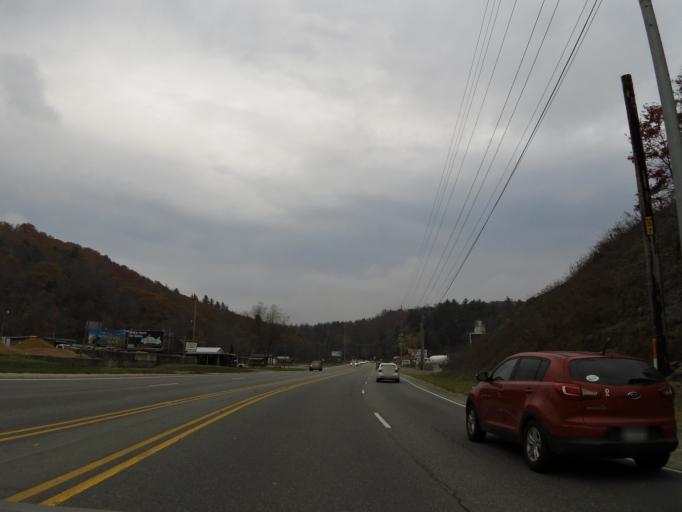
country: US
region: North Carolina
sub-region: Watauga County
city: Boone
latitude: 36.1799
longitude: -81.6474
